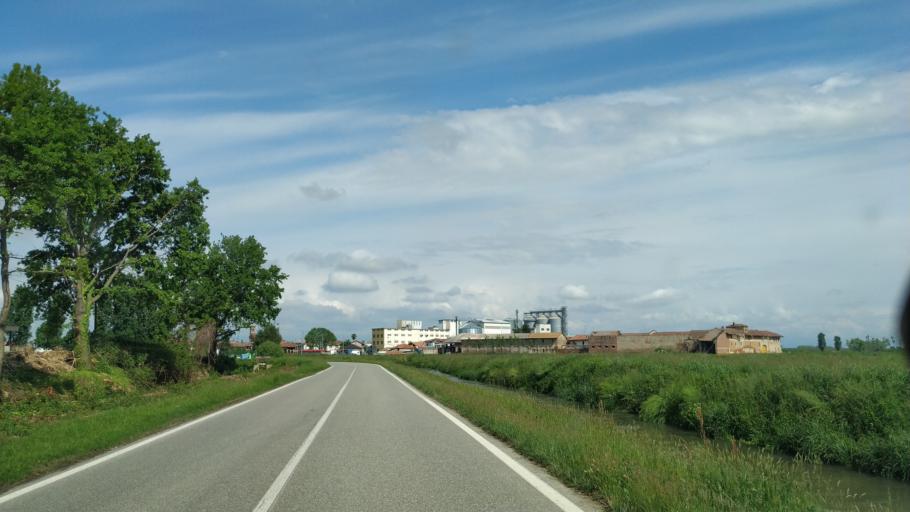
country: IT
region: Piedmont
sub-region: Provincia di Vercelli
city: Crova
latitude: 45.3259
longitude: 8.2172
